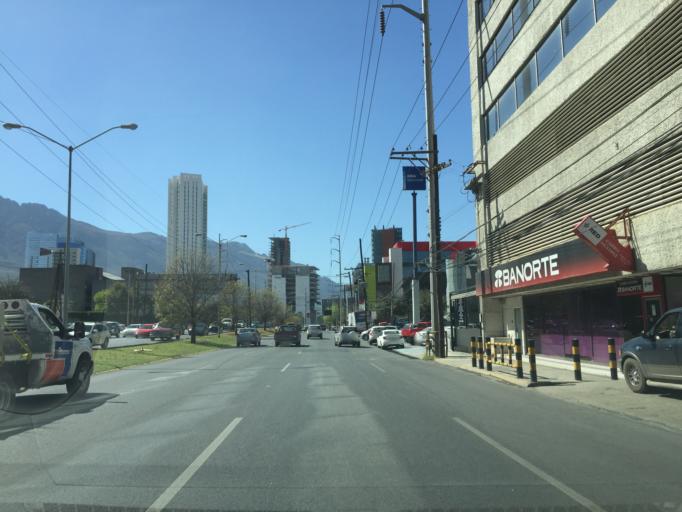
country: MX
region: Nuevo Leon
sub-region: Monterrey
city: Monterrey
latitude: 25.6537
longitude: -100.3435
